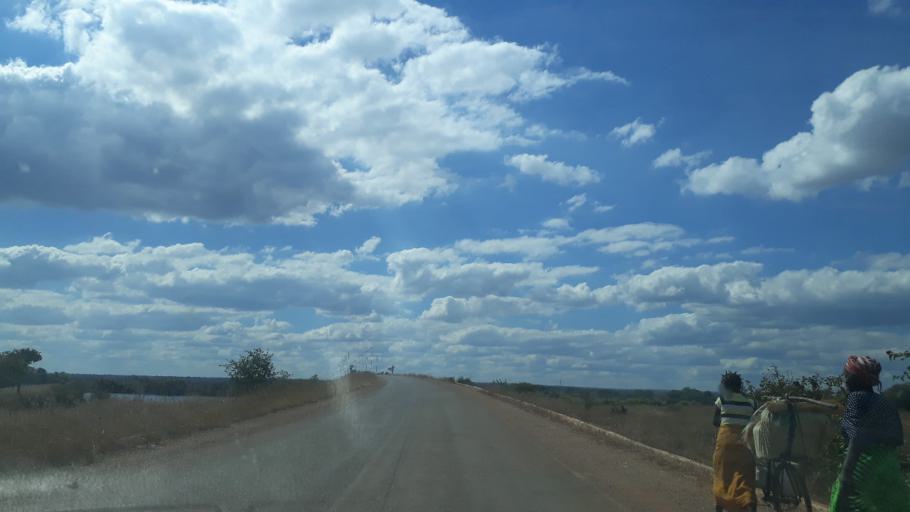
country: ZM
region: Copperbelt
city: Mufulira
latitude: -11.9884
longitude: 28.7305
